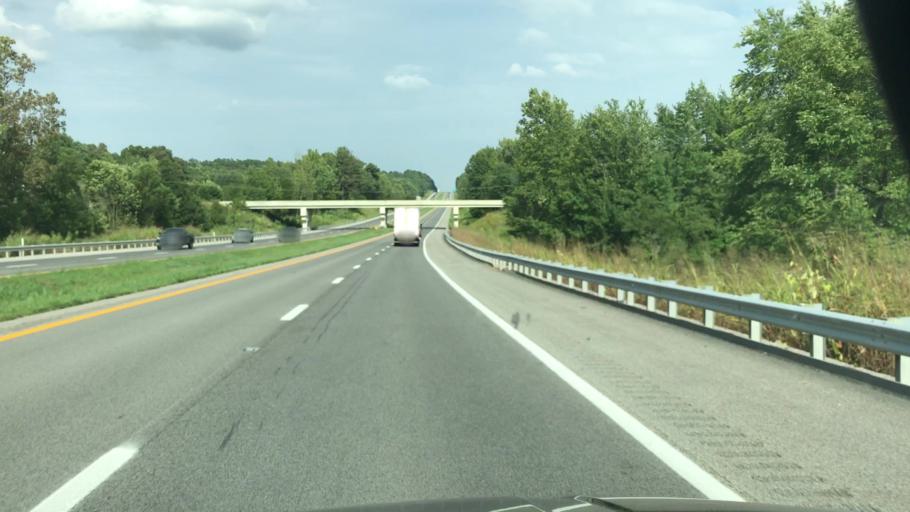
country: US
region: Kentucky
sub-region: Muhlenberg County
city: Morehead
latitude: 37.2474
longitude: -87.2388
